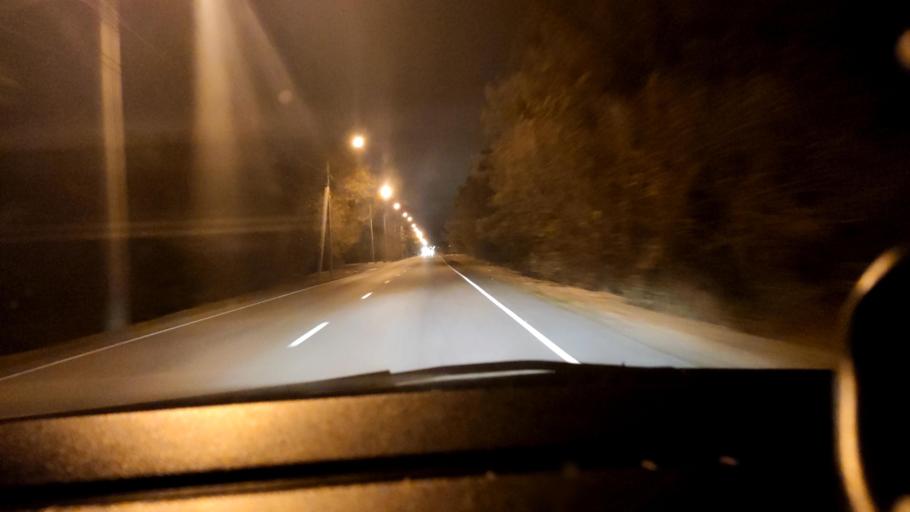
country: RU
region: Voronezj
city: Shilovo
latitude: 51.6069
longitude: 39.0423
